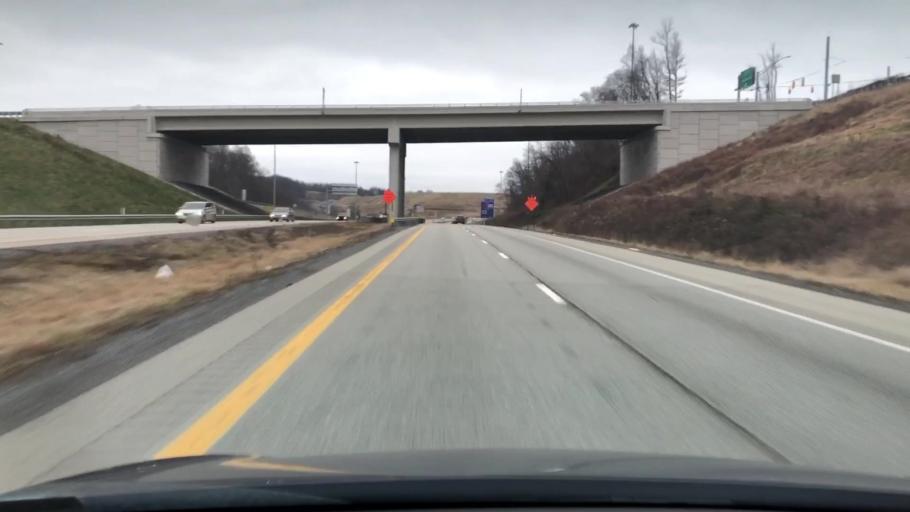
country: US
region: West Virginia
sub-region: Monongalia County
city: Star City
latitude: 39.6388
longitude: -80.0006
